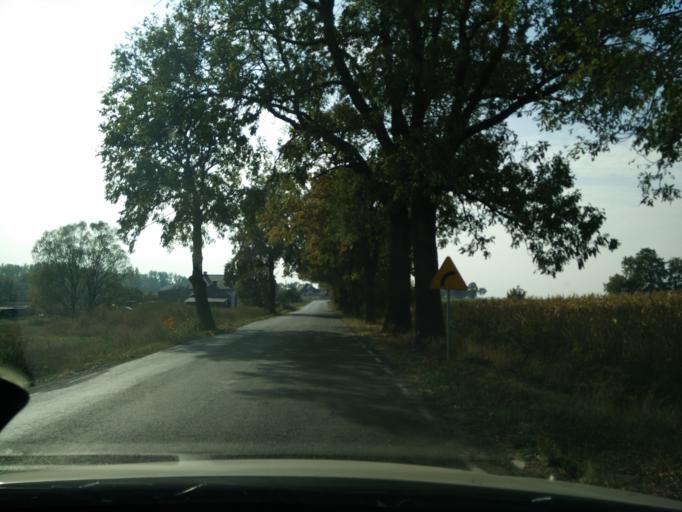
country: PL
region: Greater Poland Voivodeship
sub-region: Powiat sredzki
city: Dominowo
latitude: 52.2677
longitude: 17.3137
